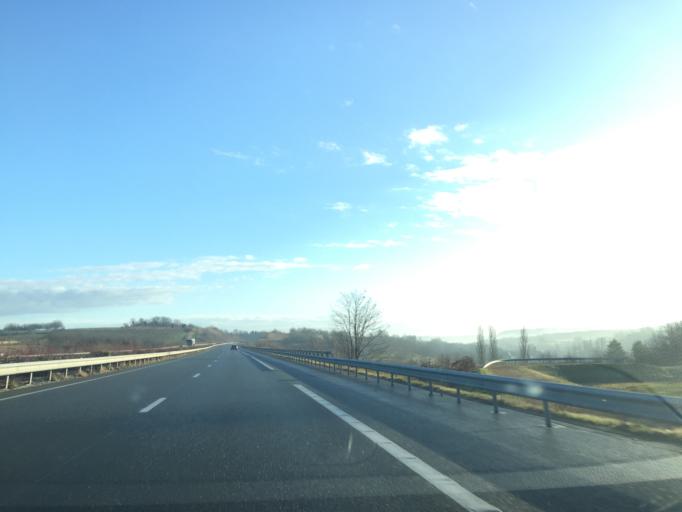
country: FR
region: Aquitaine
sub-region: Departement de la Dordogne
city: Thenon
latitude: 45.1536
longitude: 1.1081
